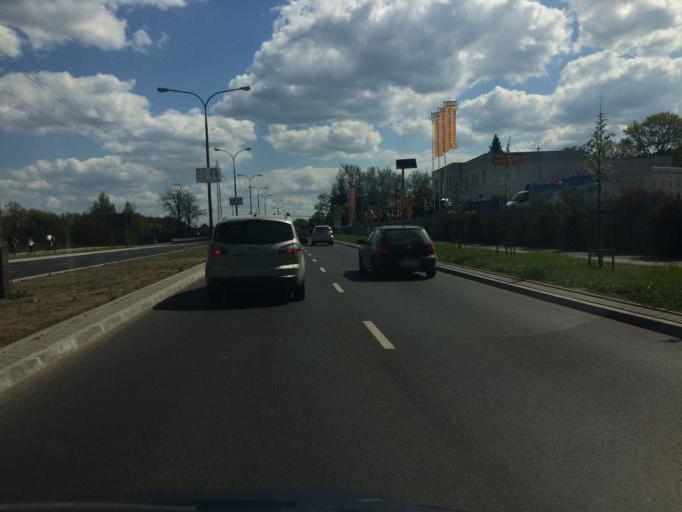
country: PL
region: Warmian-Masurian Voivodeship
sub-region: Olsztyn
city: Kortowo
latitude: 53.7737
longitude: 20.4547
